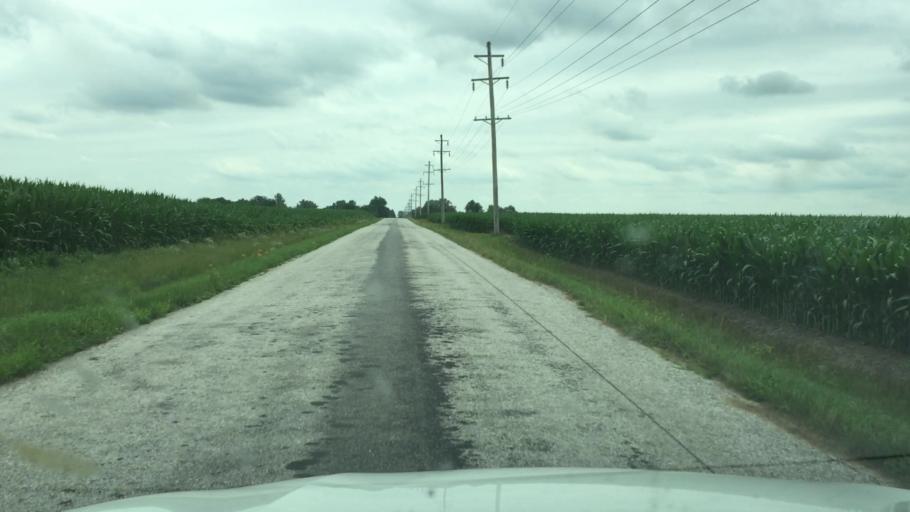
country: US
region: Illinois
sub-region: Hancock County
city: Carthage
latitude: 40.3373
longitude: -91.0824
